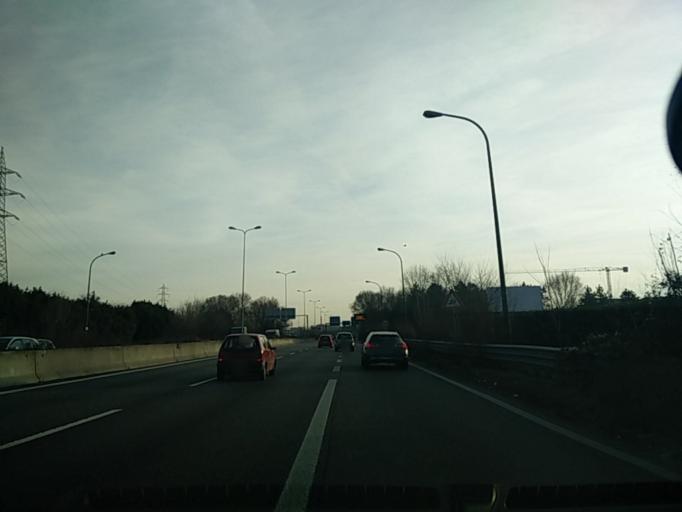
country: IT
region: Lombardy
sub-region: Citta metropolitana di Milano
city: Paderno Dugnano
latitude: 45.5686
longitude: 9.1769
